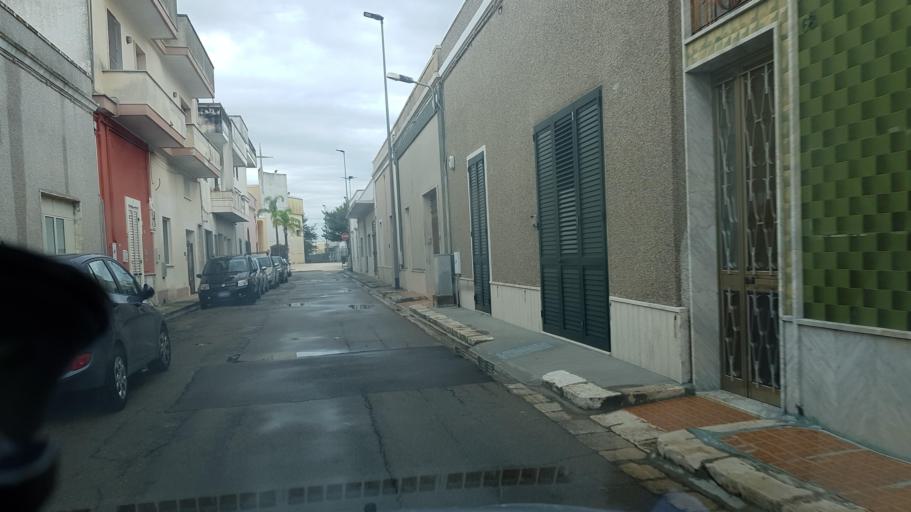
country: IT
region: Apulia
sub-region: Provincia di Lecce
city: Carmiano
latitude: 40.3477
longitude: 18.0399
